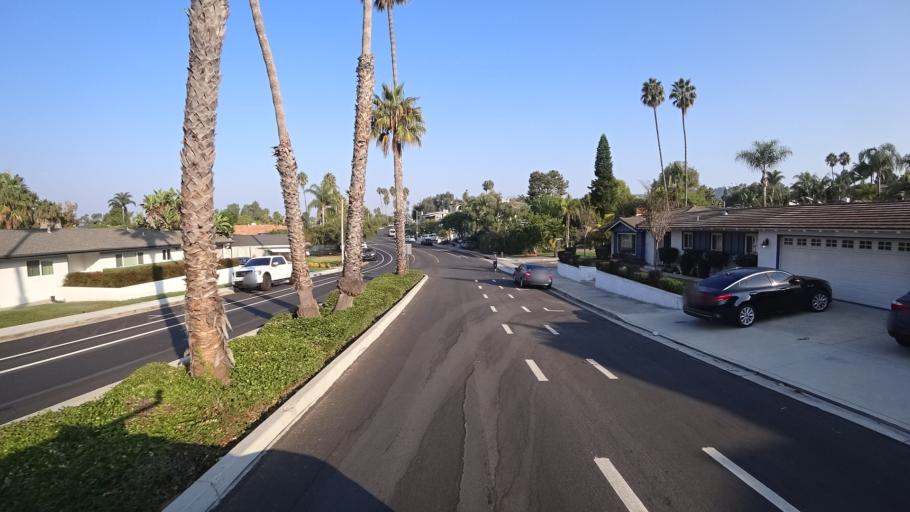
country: US
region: California
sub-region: Orange County
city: San Clemente
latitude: 33.4104
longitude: -117.6042
